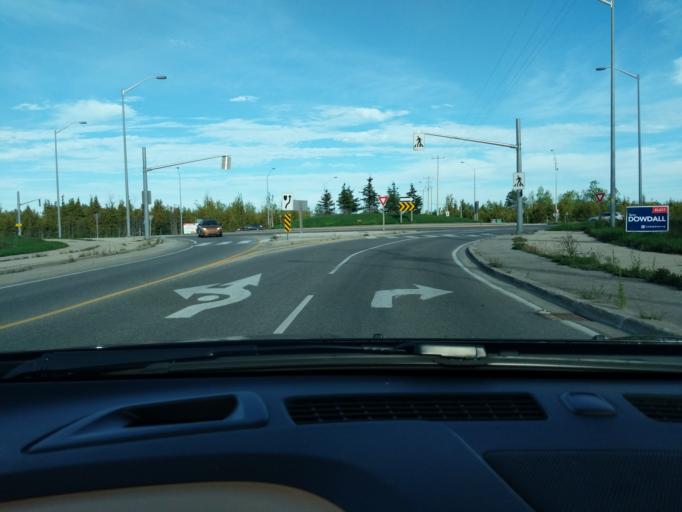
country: CA
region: Ontario
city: Collingwood
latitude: 44.4870
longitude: -80.1747
